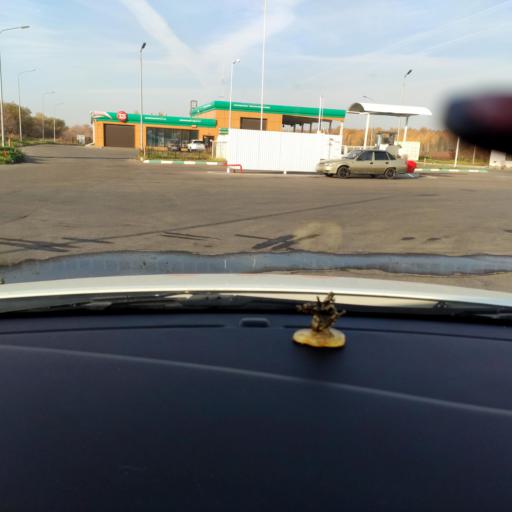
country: RU
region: Tatarstan
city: Osinovo
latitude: 55.9020
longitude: 48.9289
